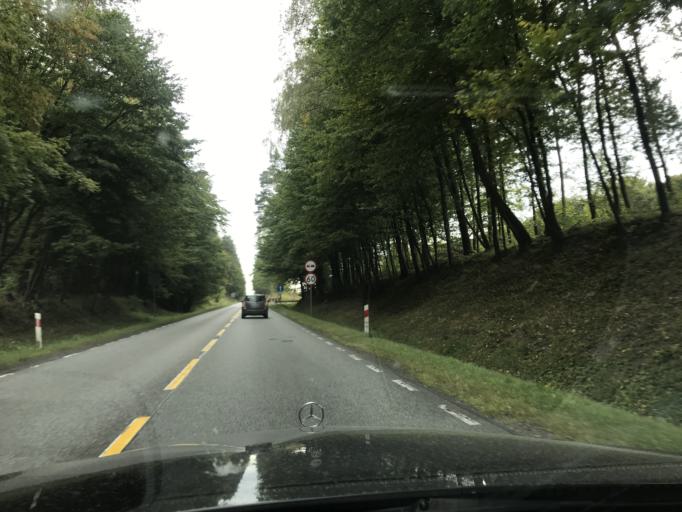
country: PL
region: Lublin Voivodeship
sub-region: Powiat krasnicki
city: Szastarka
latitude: 50.8535
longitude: 22.2864
